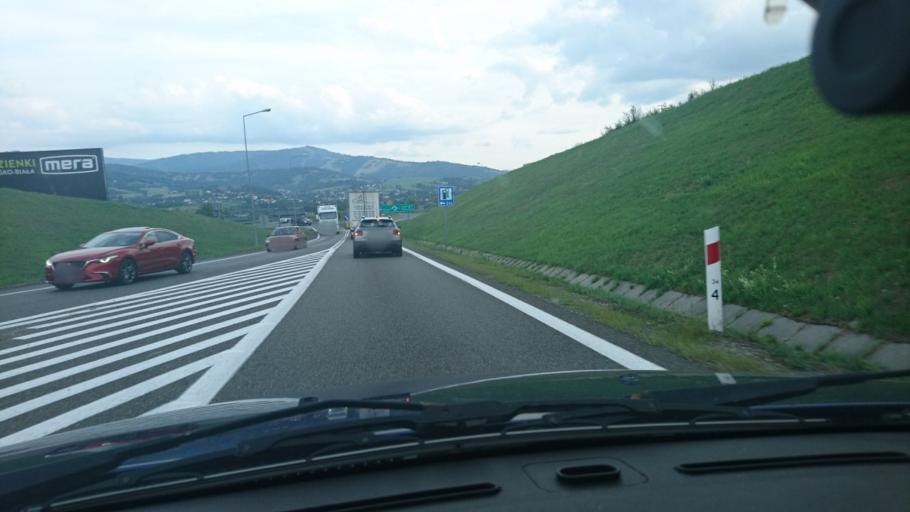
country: PL
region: Silesian Voivodeship
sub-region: Powiat zywiecki
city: Radziechowy
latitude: 49.6261
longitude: 19.1364
